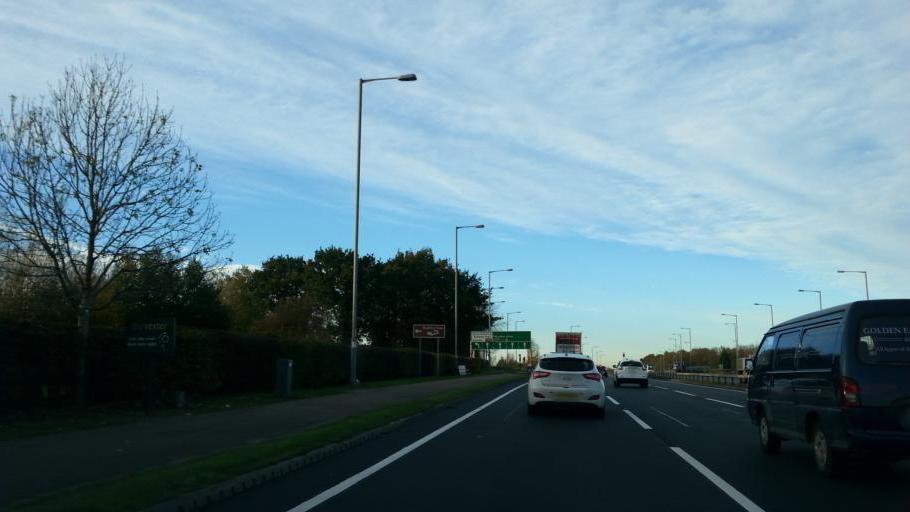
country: GB
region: England
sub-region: Northamptonshire
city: Kettering
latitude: 52.4227
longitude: -0.7289
